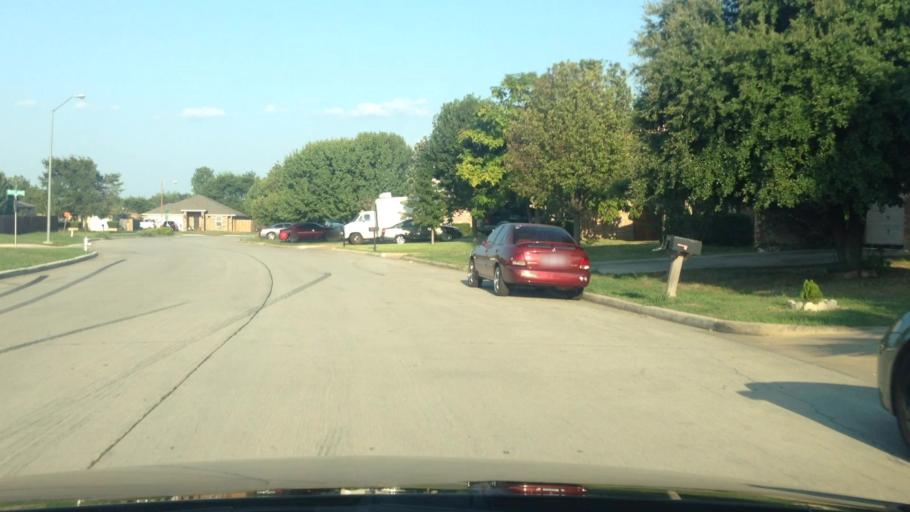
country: US
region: Texas
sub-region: Tarrant County
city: Everman
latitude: 32.6495
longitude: -97.2798
